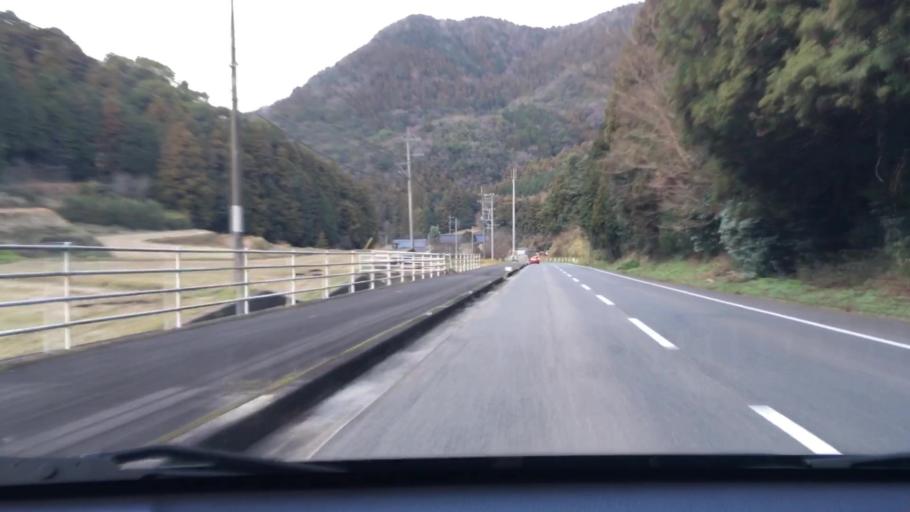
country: JP
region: Oita
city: Bungo-Takada-shi
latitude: 33.4791
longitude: 131.3862
